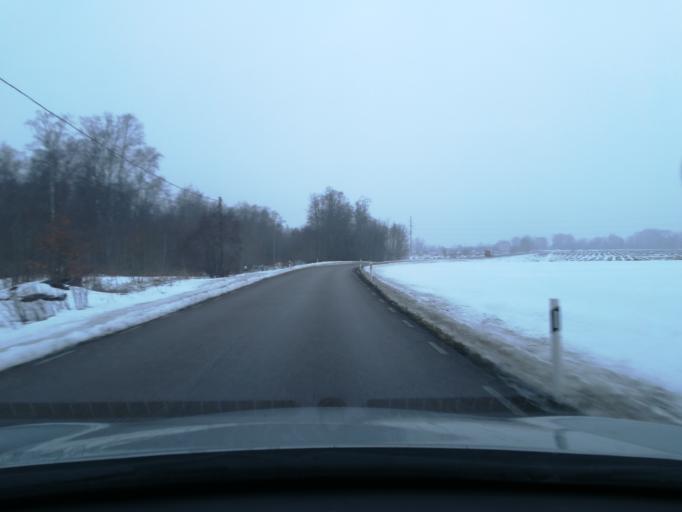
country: EE
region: Harju
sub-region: Rae vald
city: Jueri
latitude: 59.3763
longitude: 24.8965
